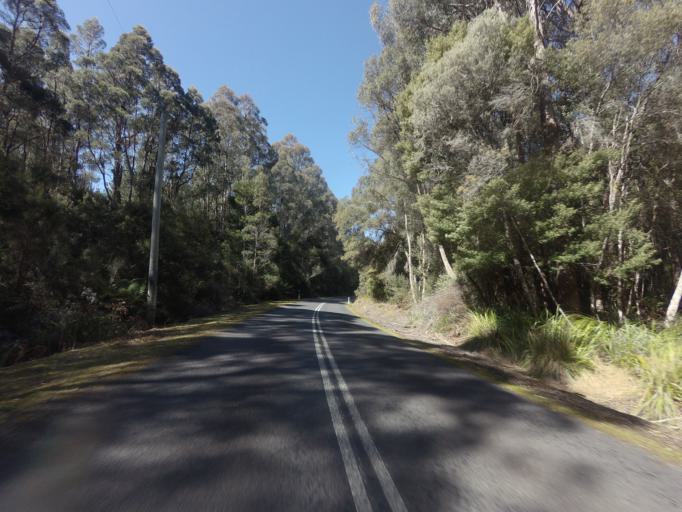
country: AU
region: Tasmania
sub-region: Derwent Valley
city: New Norfolk
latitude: -42.7675
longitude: 146.5844
